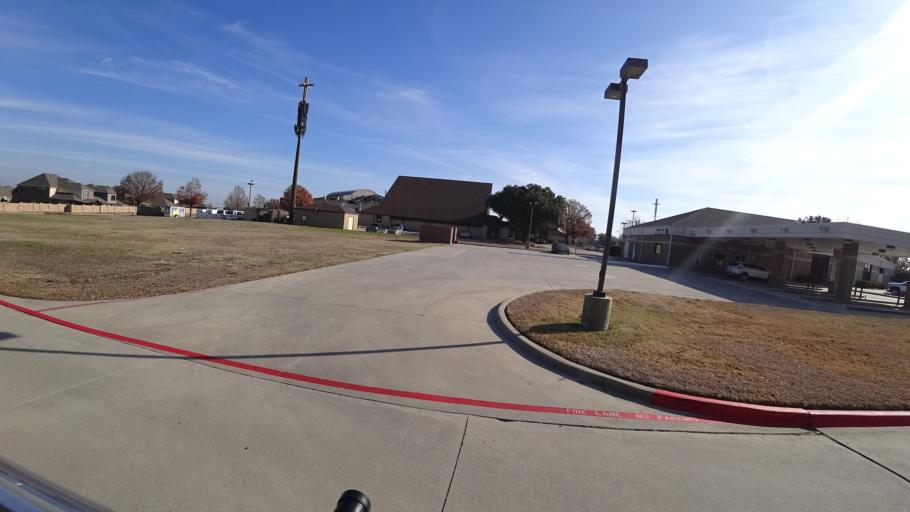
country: US
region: Texas
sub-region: Denton County
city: Lewisville
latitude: 33.0444
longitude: -97.0172
